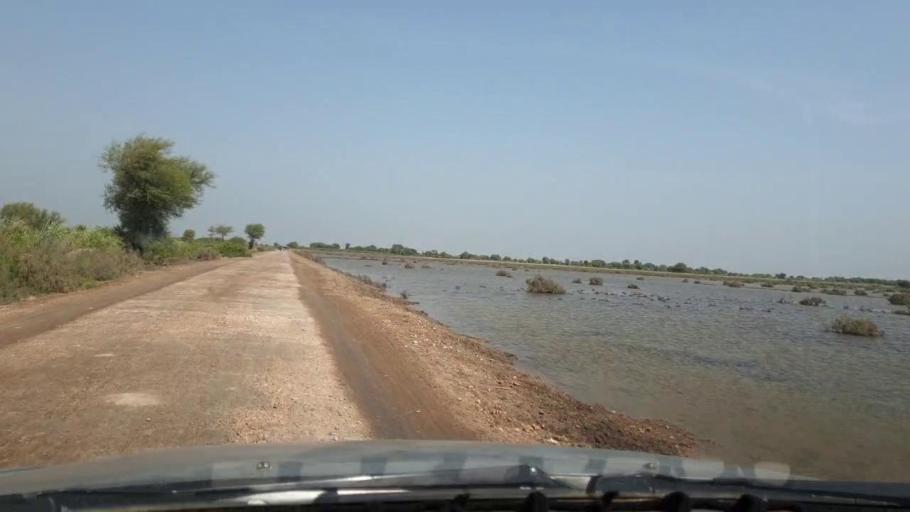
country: PK
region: Sindh
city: Tando Muhammad Khan
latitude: 25.1414
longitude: 68.6321
